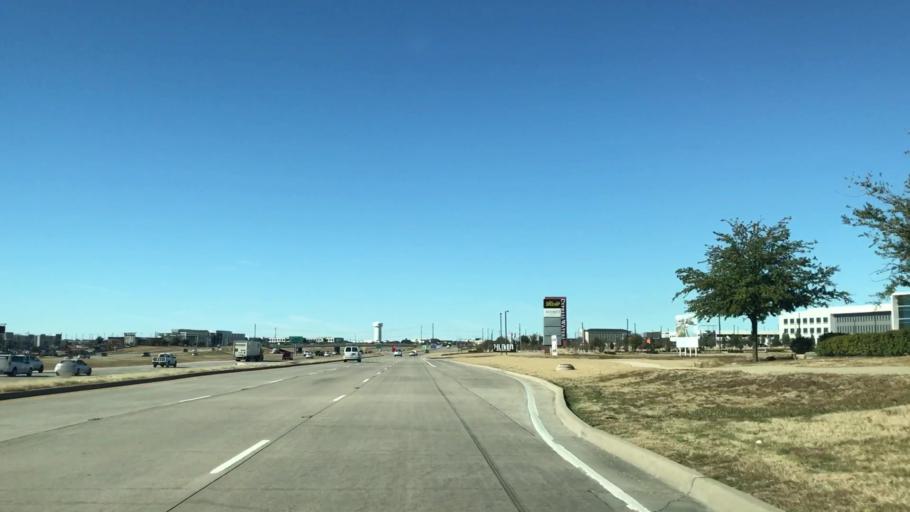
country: US
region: Texas
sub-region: Dallas County
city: Coppell
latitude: 32.9220
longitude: -96.9850
